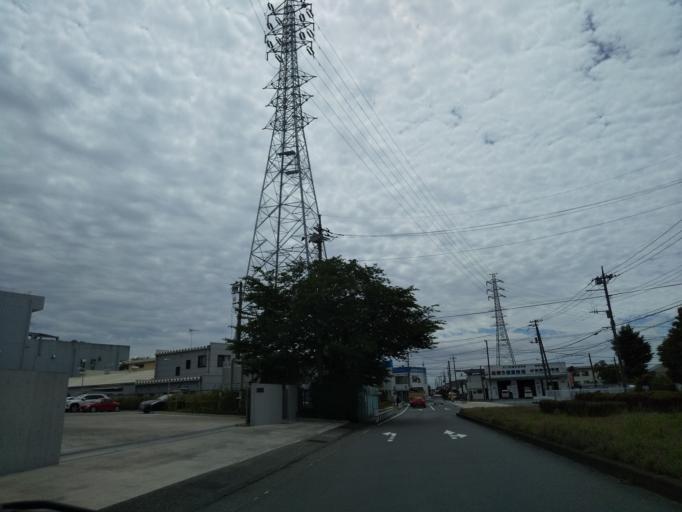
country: JP
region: Kanagawa
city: Zama
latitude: 35.5087
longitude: 139.3461
